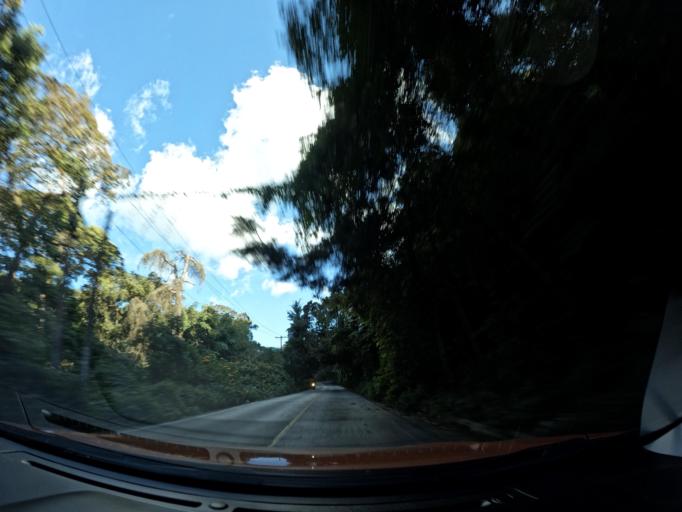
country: GT
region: Sacatepequez
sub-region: Municipio de Santa Maria de Jesus
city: Santa Maria de Jesus
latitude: 14.5124
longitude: -90.7207
